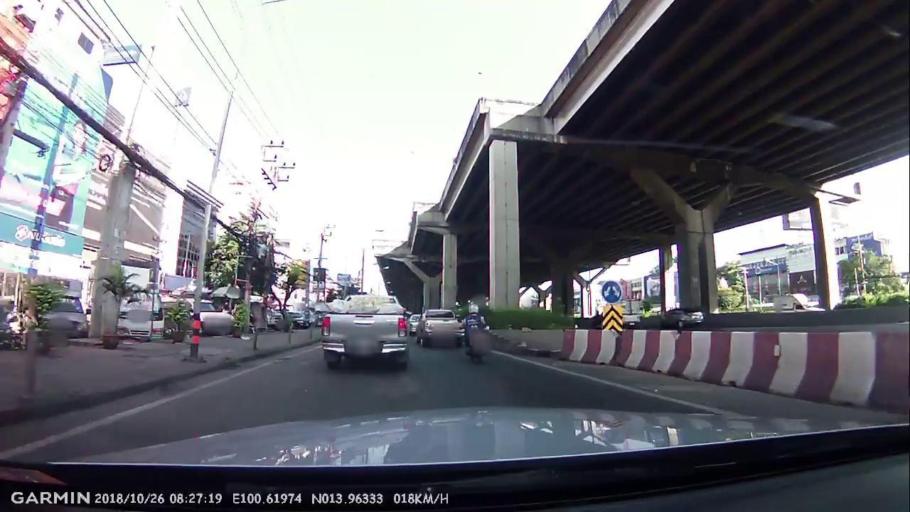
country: TH
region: Bangkok
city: Sai Mai
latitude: 13.9634
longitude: 100.6197
